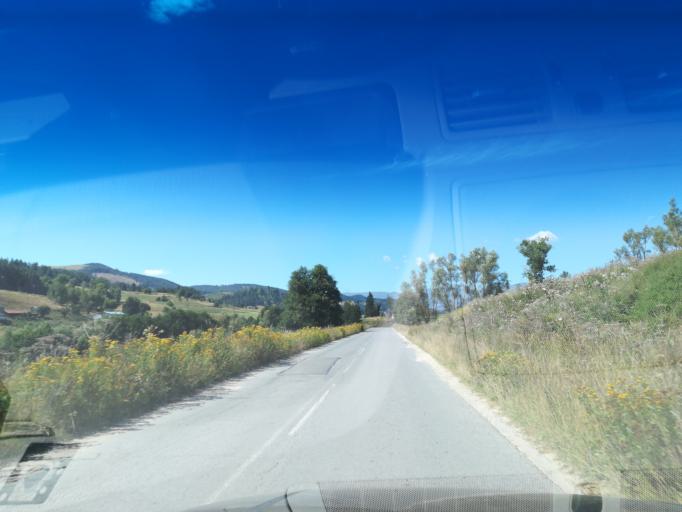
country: BG
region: Sofiya
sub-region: Obshtina Koprivshtitsa
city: Koprivshtitsa
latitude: 42.6107
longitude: 24.3758
